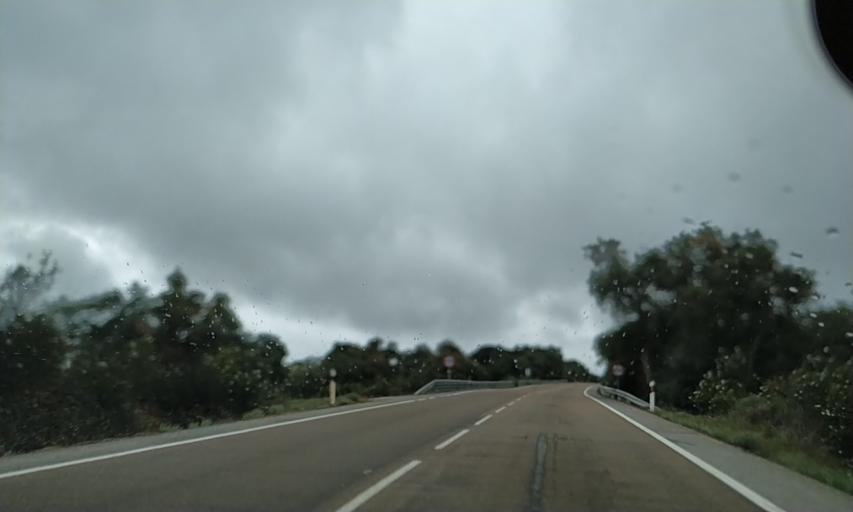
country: ES
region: Extremadura
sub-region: Provincia de Badajoz
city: Puebla de Obando
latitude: 39.2381
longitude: -6.5643
